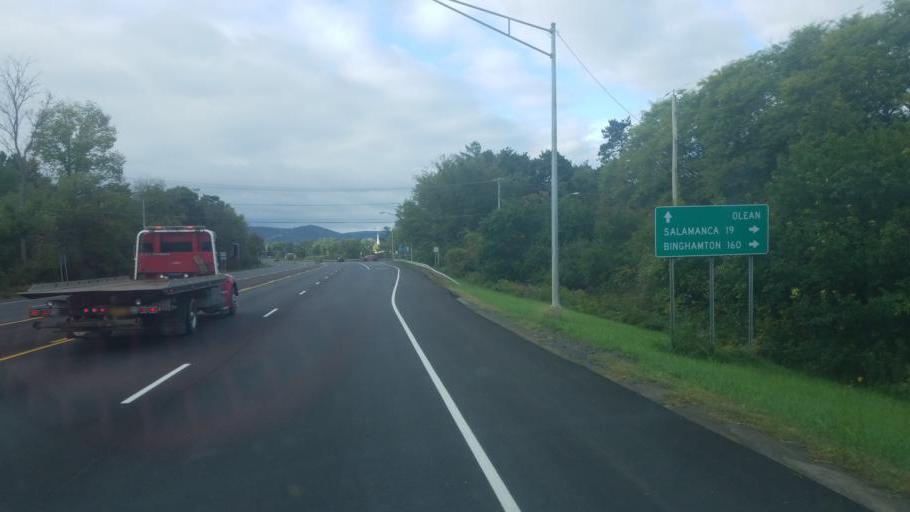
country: US
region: New York
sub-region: Cattaraugus County
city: Olean
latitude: 42.0992
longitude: -78.4245
